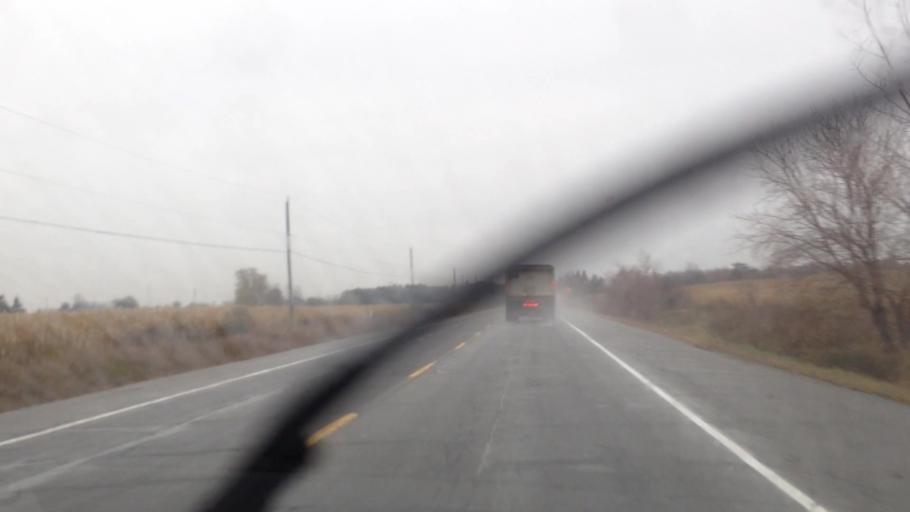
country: CA
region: Ontario
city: Clarence-Rockland
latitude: 45.3493
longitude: -75.3677
